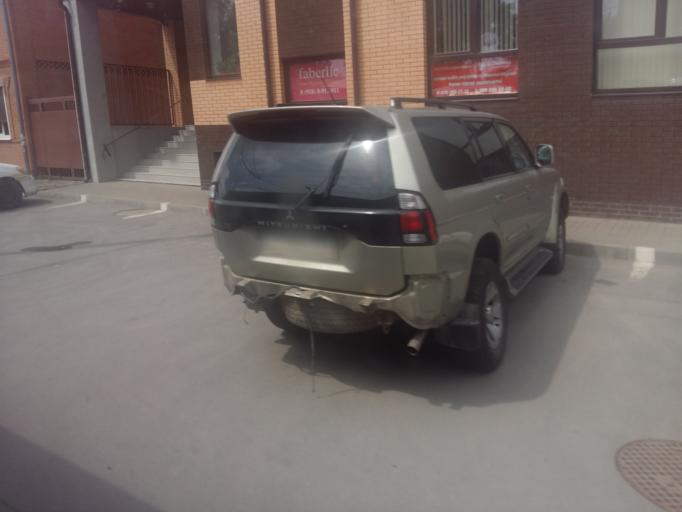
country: RU
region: Rostov
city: Imeni Chkalova
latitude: 47.2819
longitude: 39.7522
